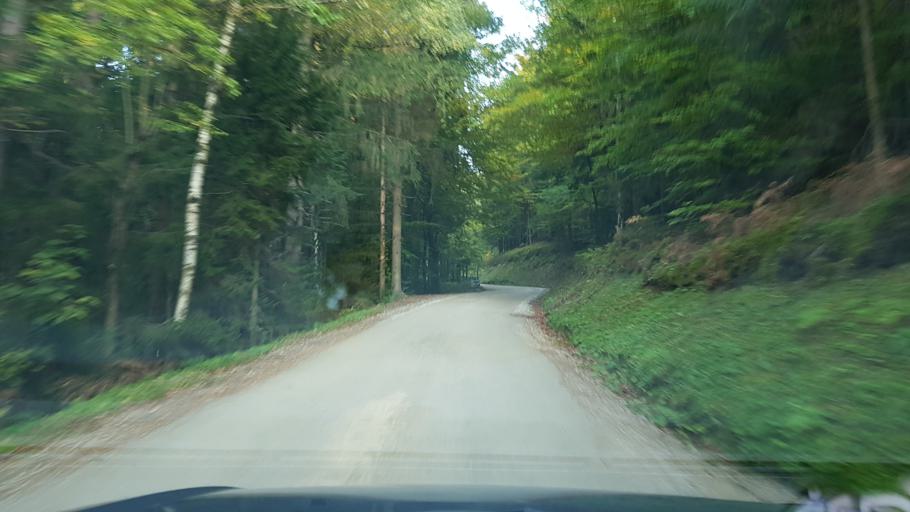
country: SI
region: Slovenj Gradec
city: Smartno pri Slovenj Gradcu
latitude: 46.5124
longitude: 15.1142
